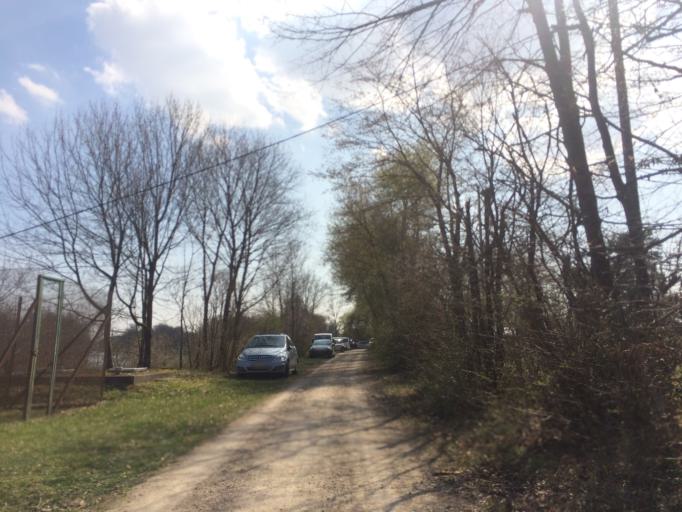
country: DE
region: Bavaria
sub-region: Swabia
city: Gersthofen
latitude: 48.4072
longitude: 10.8877
